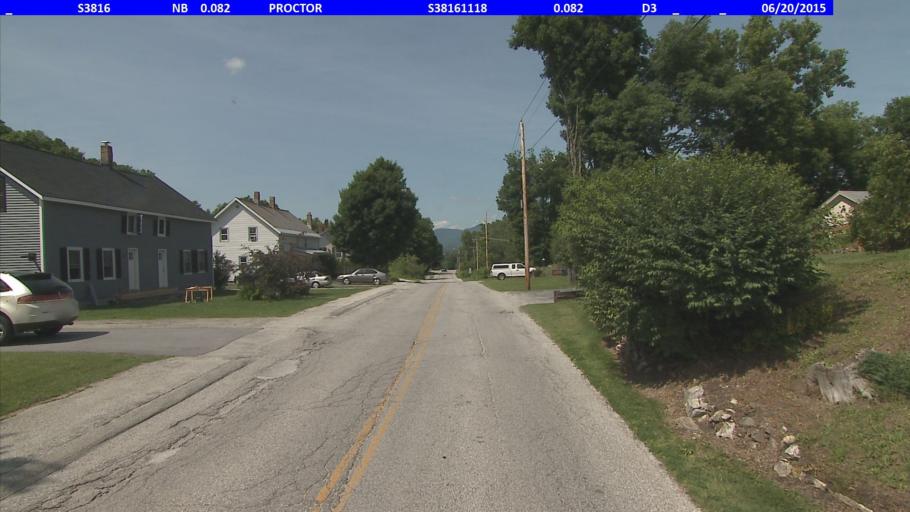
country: US
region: Vermont
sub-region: Rutland County
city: West Rutland
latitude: 43.6642
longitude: -73.0387
